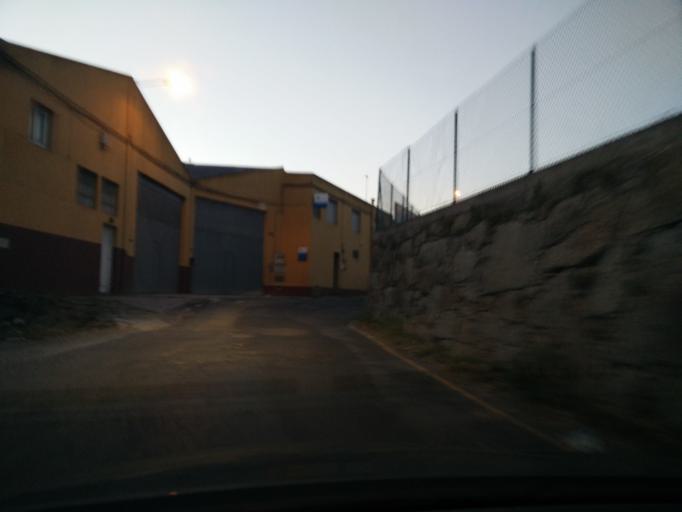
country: ES
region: Galicia
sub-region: Provincia da Coruna
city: A Coruna
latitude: 43.3475
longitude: -8.4223
